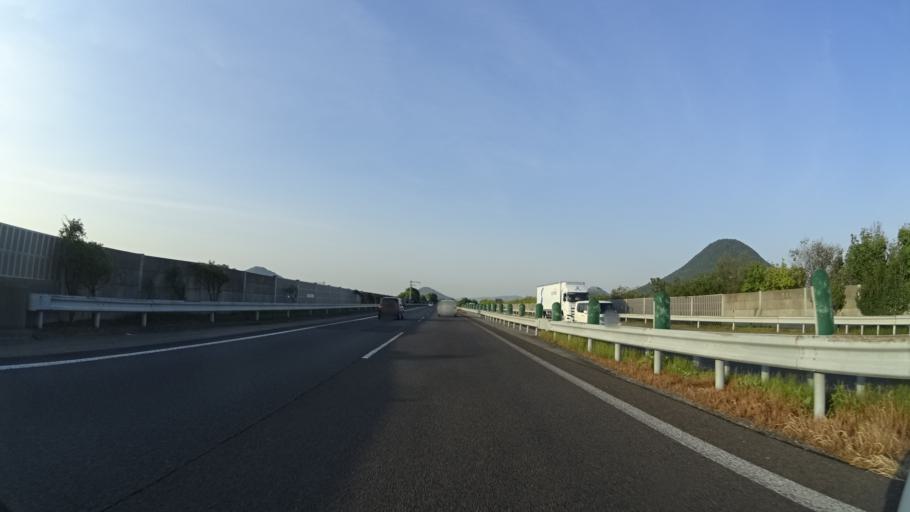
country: JP
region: Kagawa
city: Marugame
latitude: 34.2647
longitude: 133.8199
